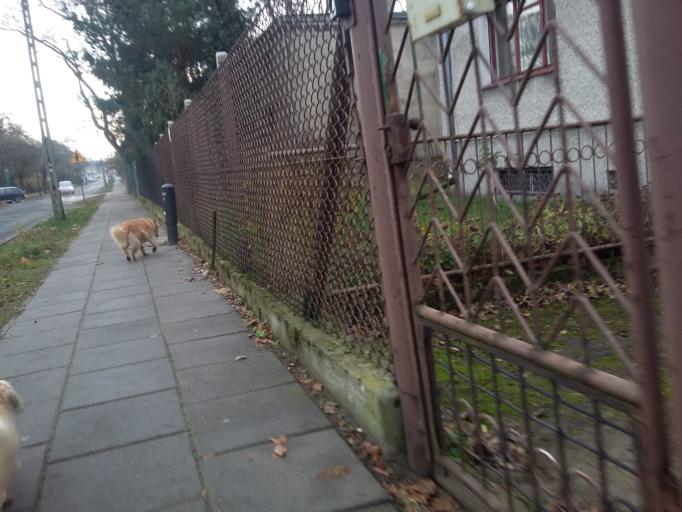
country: PL
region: Lodz Voivodeship
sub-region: Powiat pabianicki
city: Ksawerow
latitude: 51.7130
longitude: 19.4240
